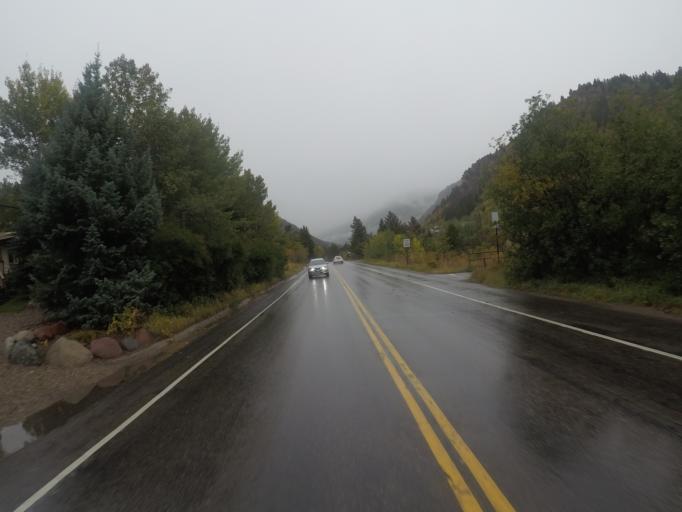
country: US
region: Colorado
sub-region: Pitkin County
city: Aspen
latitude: 39.1871
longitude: -106.8522
